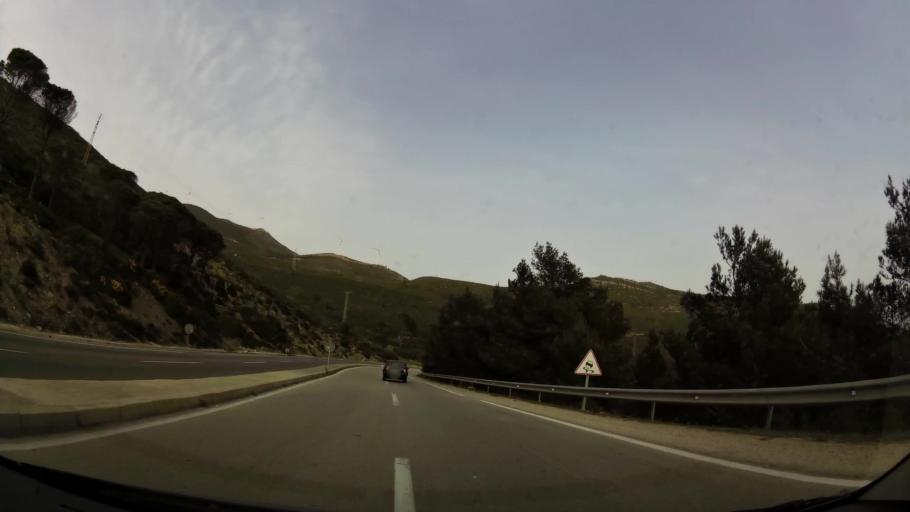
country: MA
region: Tanger-Tetouan
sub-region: Tetouan
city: Saddina
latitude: 35.5603
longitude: -5.5716
